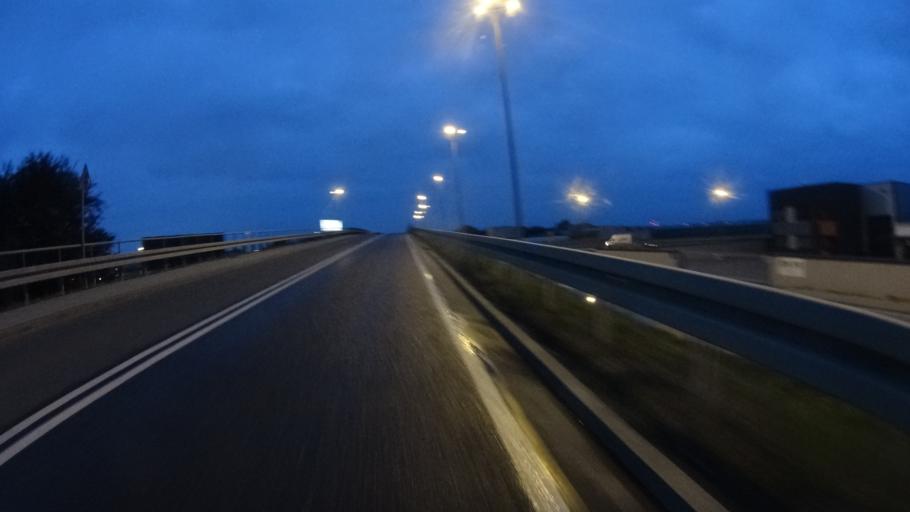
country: PL
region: Masovian Voivodeship
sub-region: Warszawa
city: Ursus
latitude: 52.2281
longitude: 20.8783
